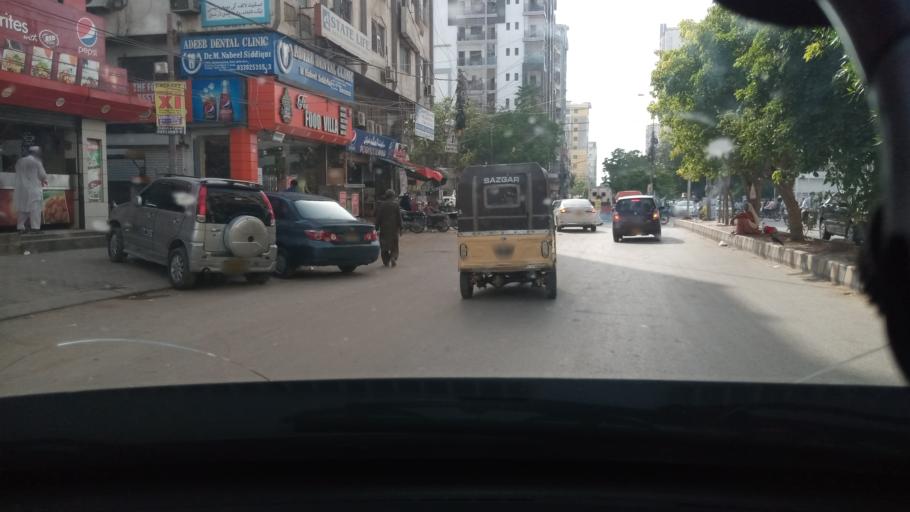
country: PK
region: Sindh
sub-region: Karachi District
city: Karachi
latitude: 24.8734
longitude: 67.0570
